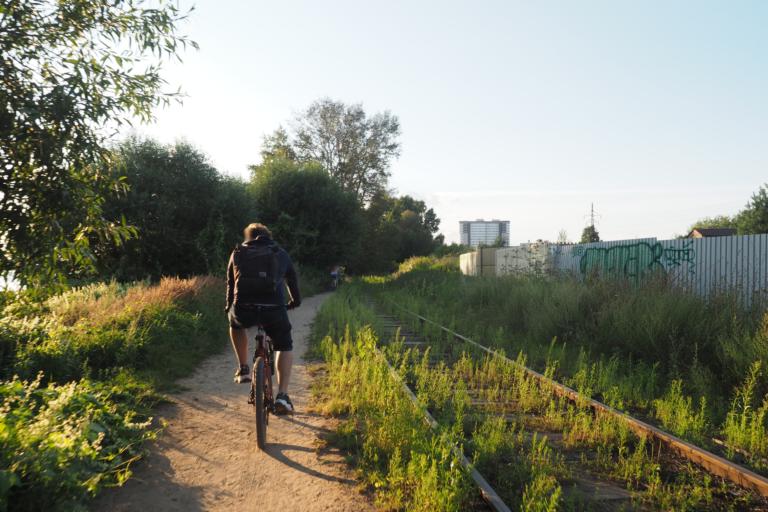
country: RU
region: Moskovskaya
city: Staraya Kupavna
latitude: 55.7993
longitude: 38.1760
